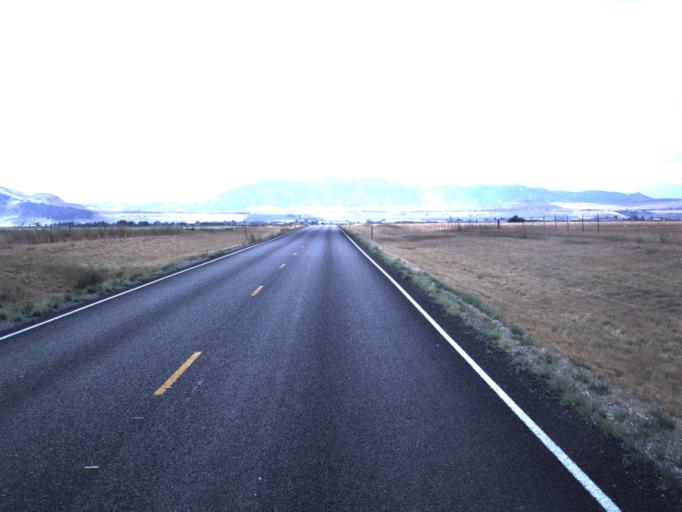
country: US
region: Utah
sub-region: Cache County
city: Lewiston
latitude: 41.9250
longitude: -111.8659
